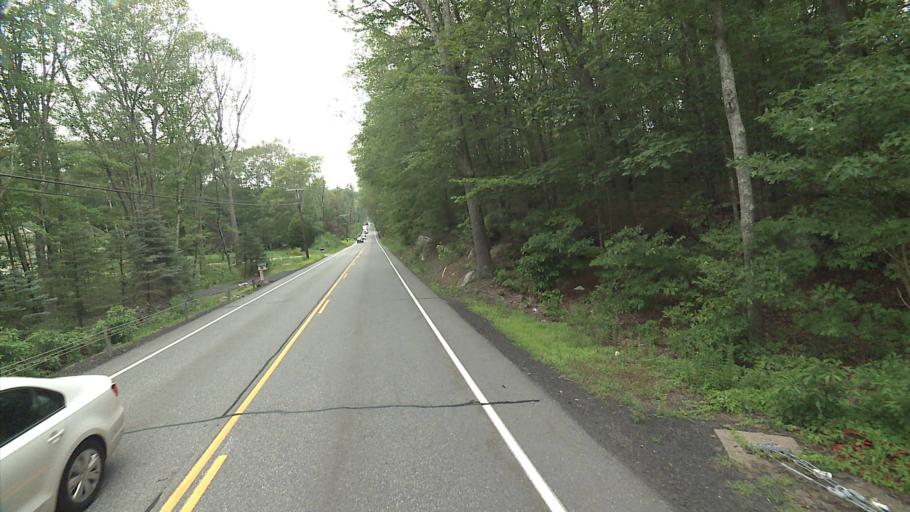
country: US
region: Connecticut
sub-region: Tolland County
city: Storrs
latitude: 41.8663
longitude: -72.1976
